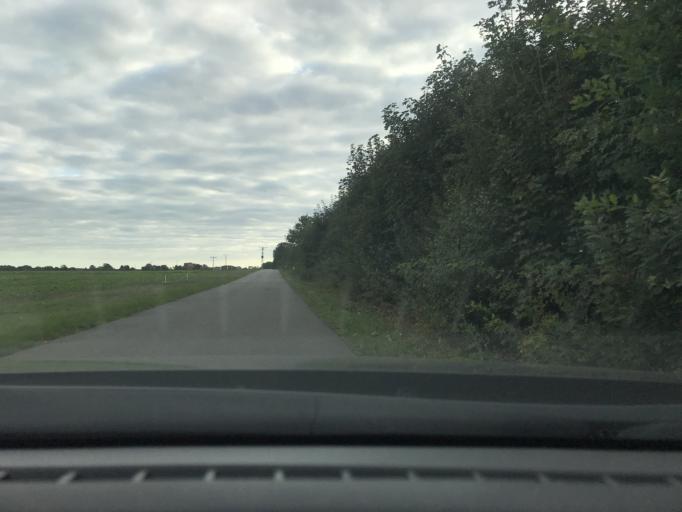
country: DE
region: Lower Saxony
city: Suderburg
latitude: 52.9082
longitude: 10.4547
